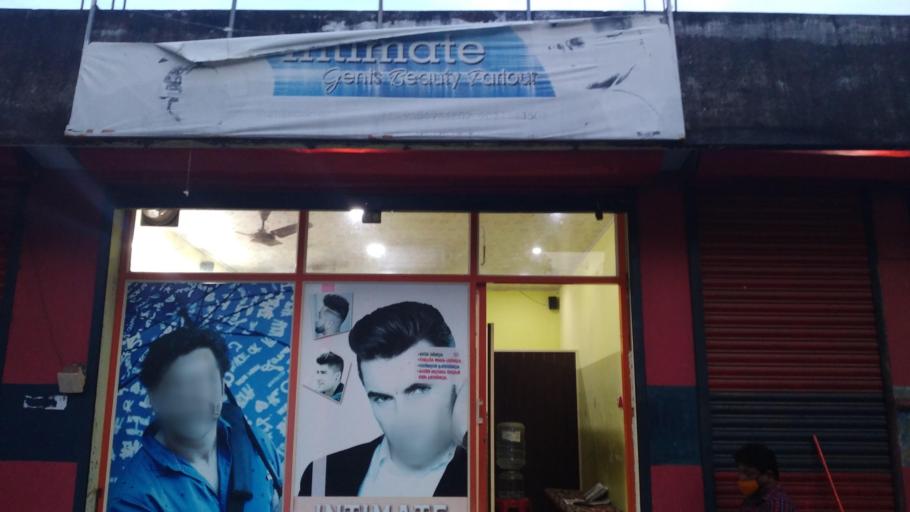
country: IN
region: Kerala
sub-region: Alappuzha
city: Kayankulam
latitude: 9.2590
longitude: 76.4499
